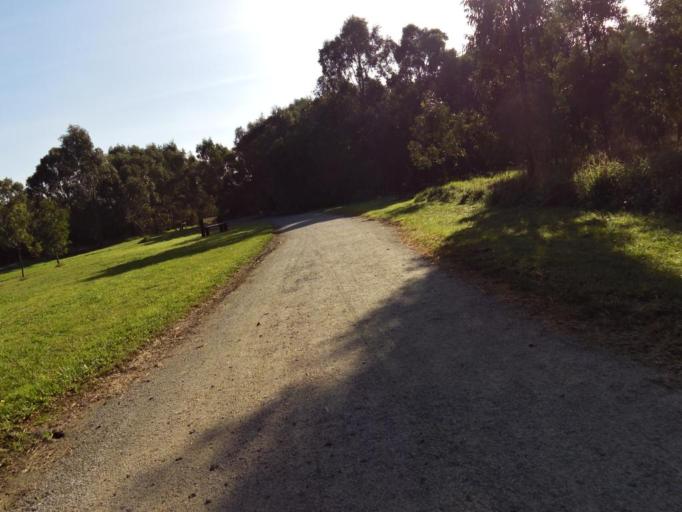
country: AU
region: Victoria
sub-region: Kingston
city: Dingley Village
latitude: -37.9934
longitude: 145.1222
